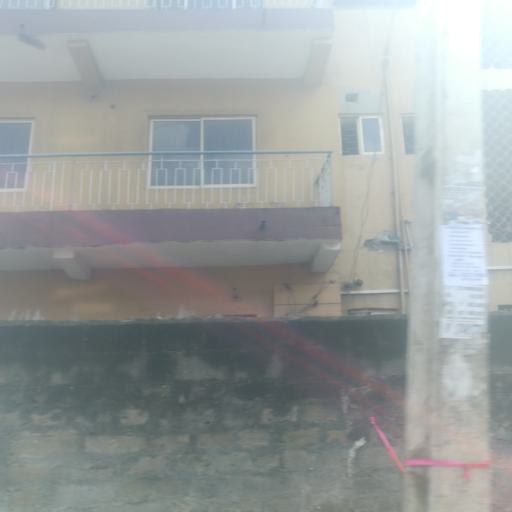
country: NG
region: Lagos
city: Ojota
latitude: 6.6007
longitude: 3.3893
